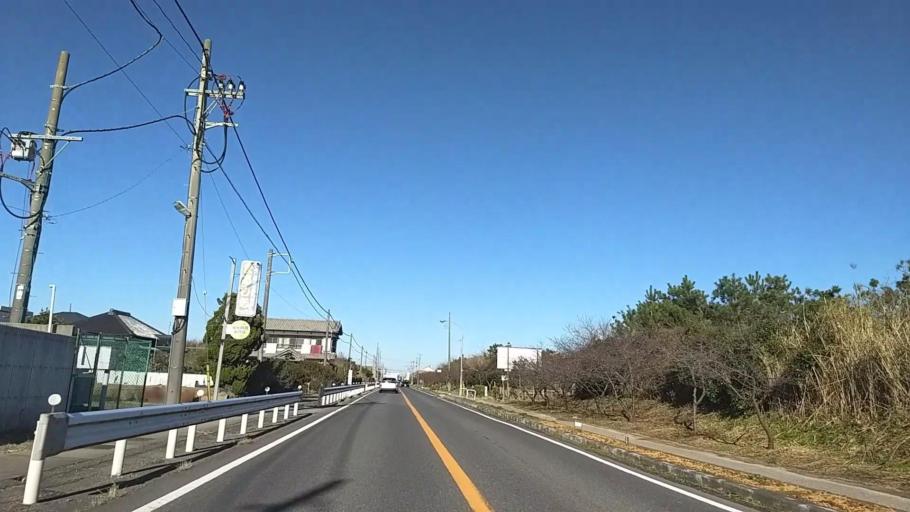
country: JP
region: Chiba
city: Togane
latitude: 35.4684
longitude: 140.4111
